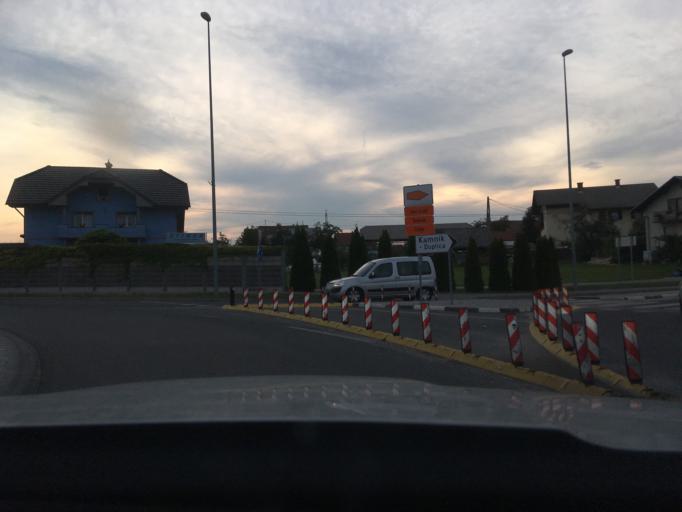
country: SI
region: Kamnik
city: Smarca
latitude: 46.1989
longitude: 14.5941
